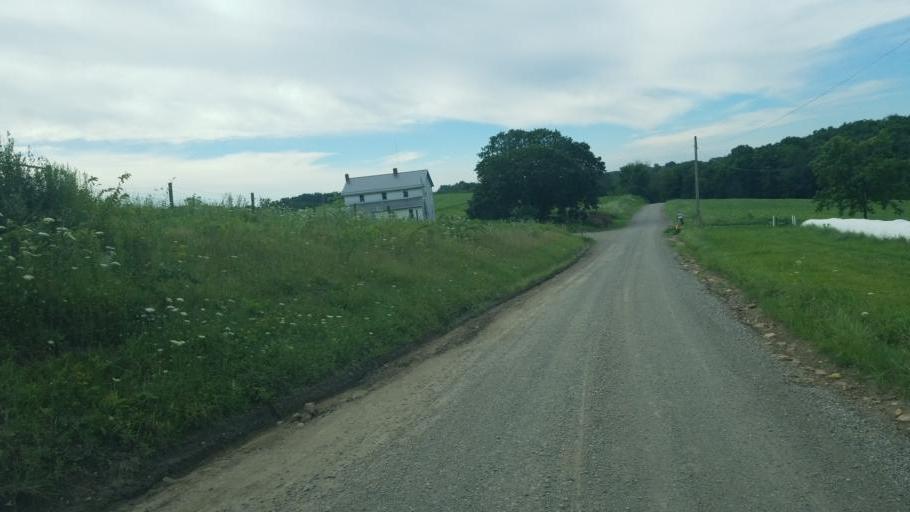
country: US
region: Ohio
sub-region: Holmes County
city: Millersburg
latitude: 40.4970
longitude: -81.8489
